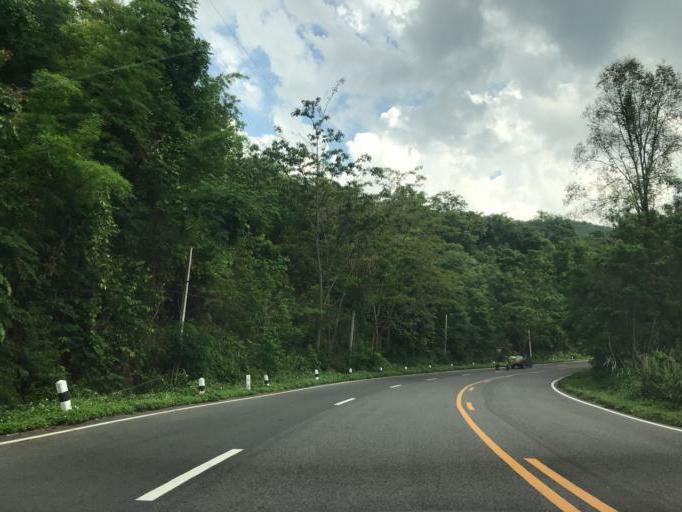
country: TH
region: Phayao
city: Phayao
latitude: 19.0747
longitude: 99.8157
